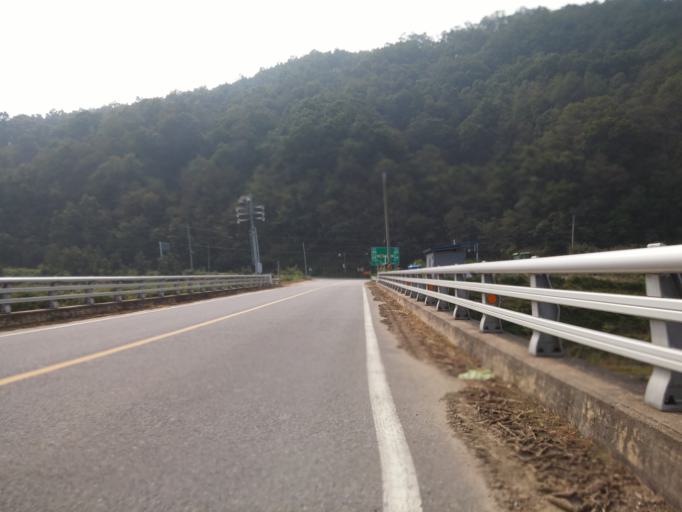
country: KR
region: Chungcheongbuk-do
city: Yong-dong
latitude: 36.3491
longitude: 127.8147
